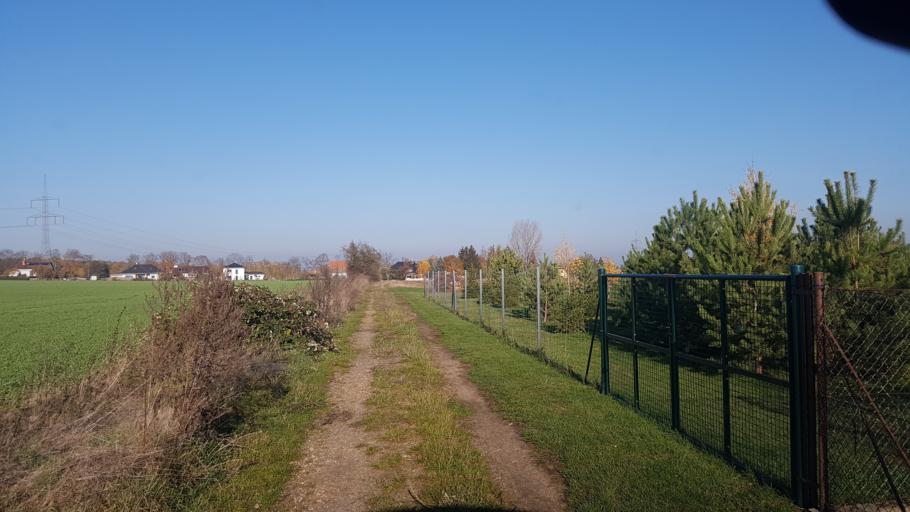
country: DE
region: Brandenburg
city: Doberlug-Kirchhain
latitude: 51.6336
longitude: 13.5434
